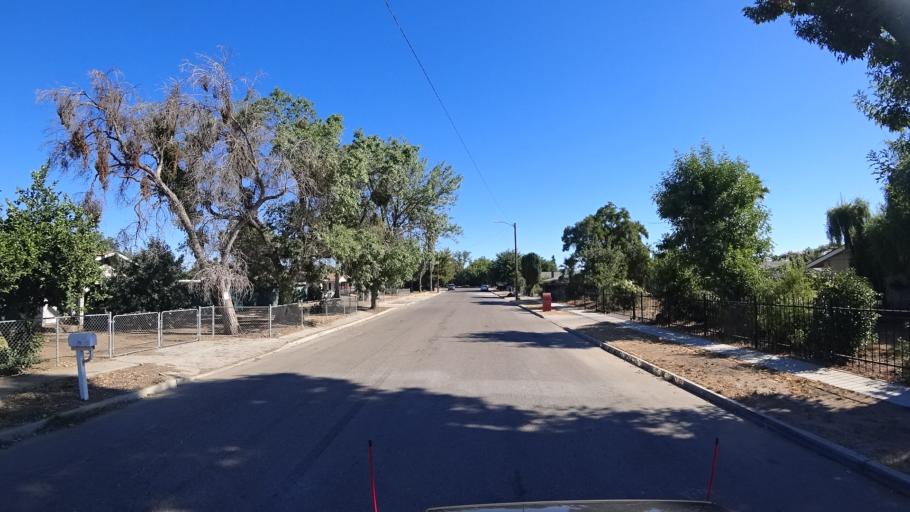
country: US
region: California
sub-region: Fresno County
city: West Park
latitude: 36.7599
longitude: -119.8378
